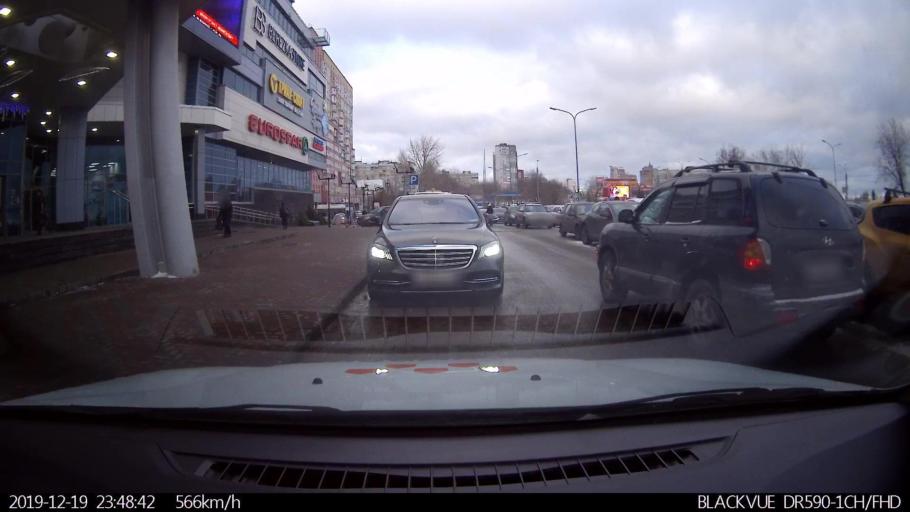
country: RU
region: Vologda
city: Cherepovets
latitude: 58.7802
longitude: 37.7358
